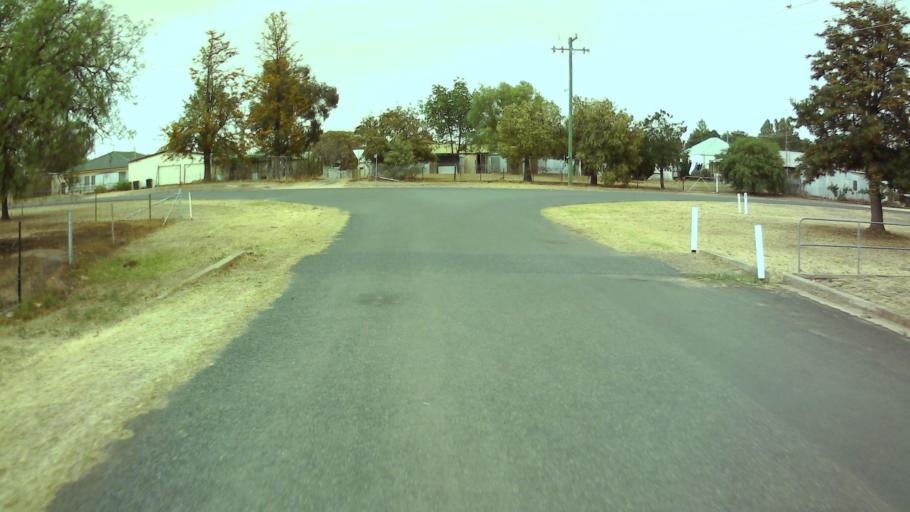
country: AU
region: New South Wales
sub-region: Weddin
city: Grenfell
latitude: -33.8905
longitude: 148.1643
